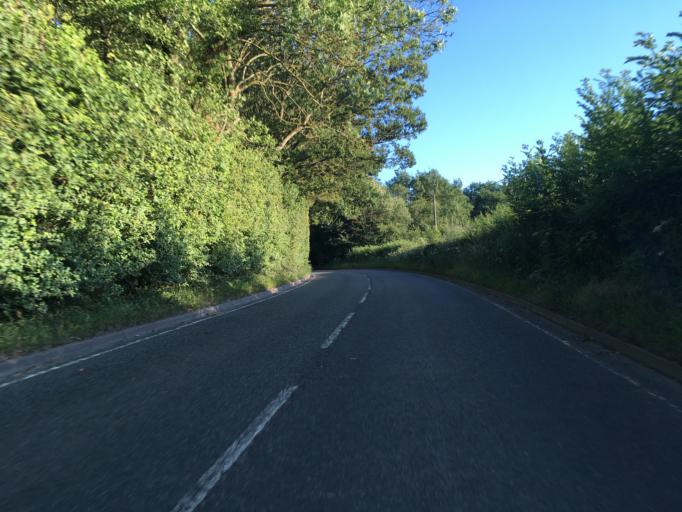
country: GB
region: England
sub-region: Hampshire
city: Tadley
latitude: 51.3796
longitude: -1.1524
